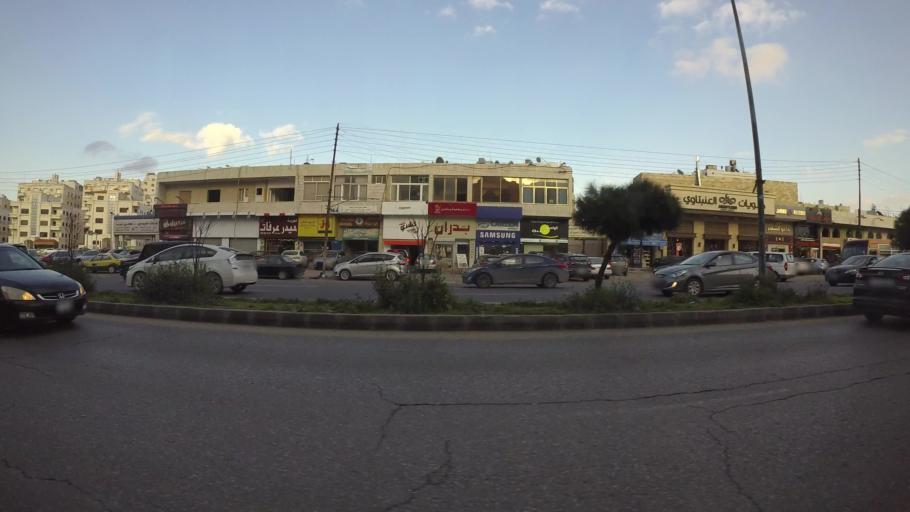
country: JO
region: Amman
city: Al Jubayhah
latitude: 31.9798
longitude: 35.8652
